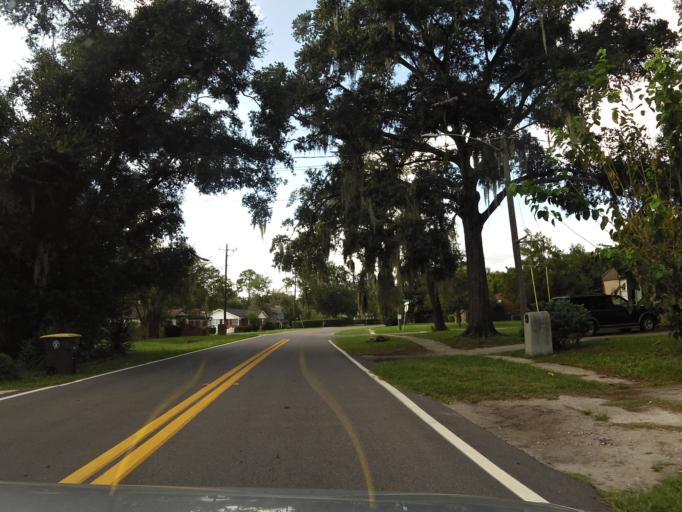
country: US
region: Florida
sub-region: Clay County
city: Bellair-Meadowbrook Terrace
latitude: 30.2691
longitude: -81.7276
